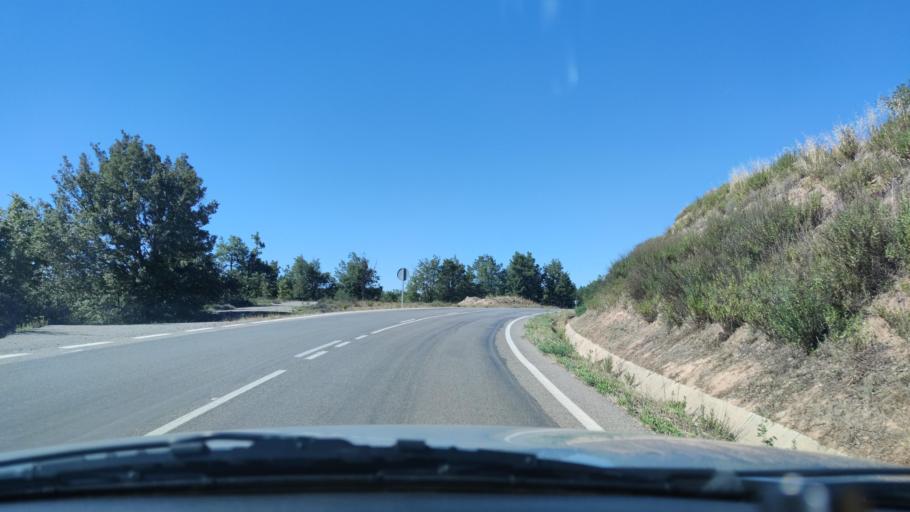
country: ES
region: Catalonia
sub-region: Provincia de Lleida
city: Solsona
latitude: 41.9302
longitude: 1.4957
